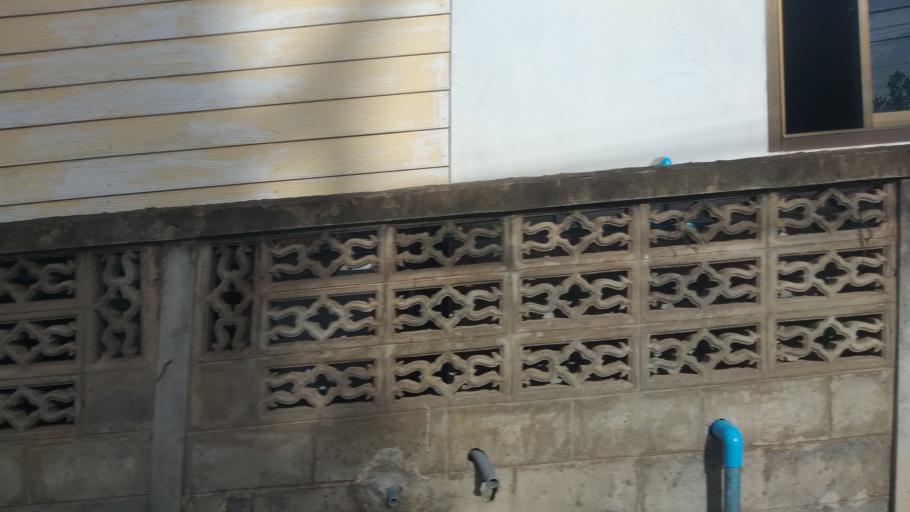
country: TH
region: Chaiyaphum
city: Ban Thaen
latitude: 16.4098
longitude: 102.3532
